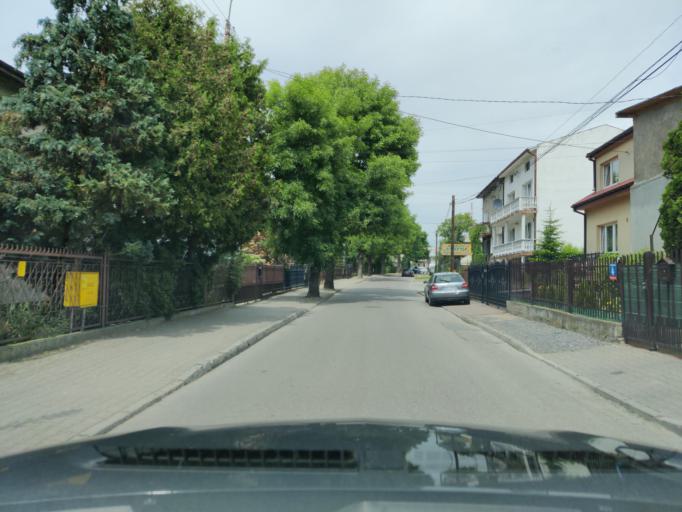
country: PL
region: Masovian Voivodeship
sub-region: Powiat wyszkowski
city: Wyszkow
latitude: 52.5951
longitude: 21.4596
